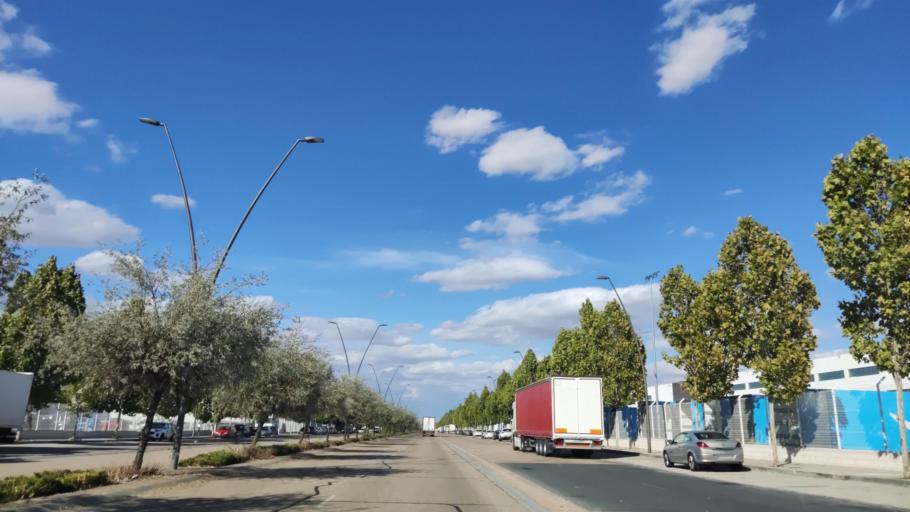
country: ES
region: Madrid
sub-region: Provincia de Madrid
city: Pinto
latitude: 40.2771
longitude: -3.6840
